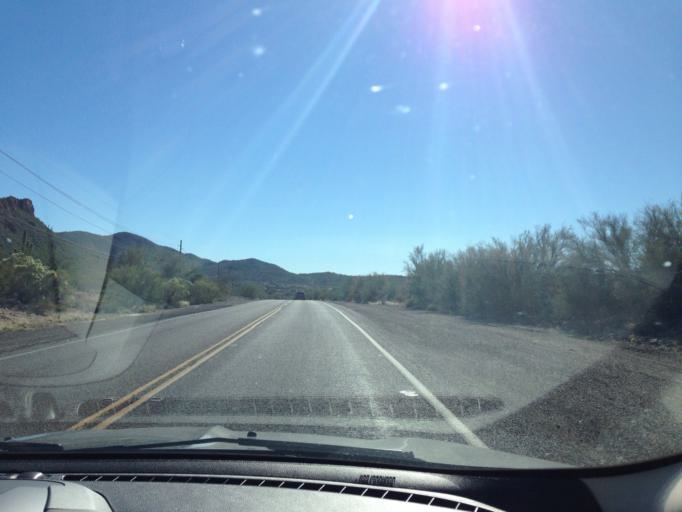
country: US
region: Arizona
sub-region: Maricopa County
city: New River
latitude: 33.8769
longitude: -112.0695
